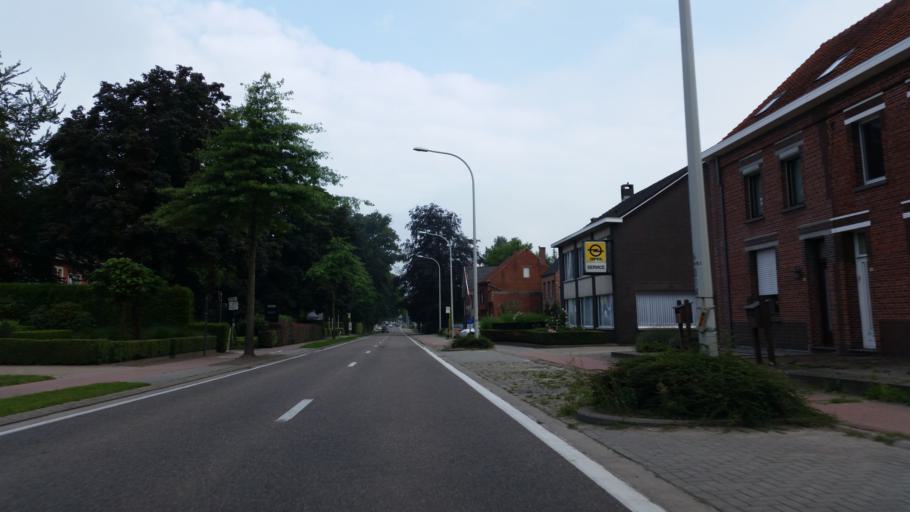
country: BE
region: Flanders
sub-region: Provincie Antwerpen
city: Hoogstraten
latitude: 51.4401
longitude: 4.7405
